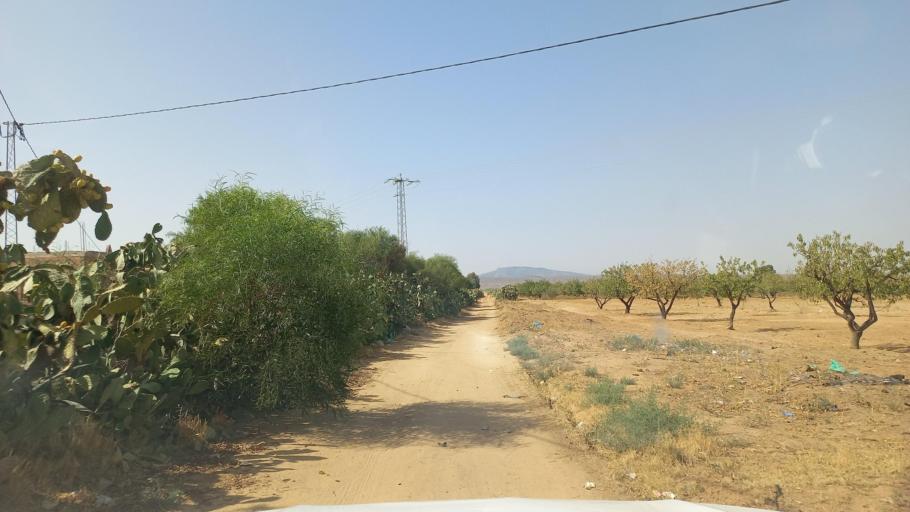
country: TN
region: Al Qasrayn
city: Kasserine
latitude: 35.2359
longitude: 9.0550
